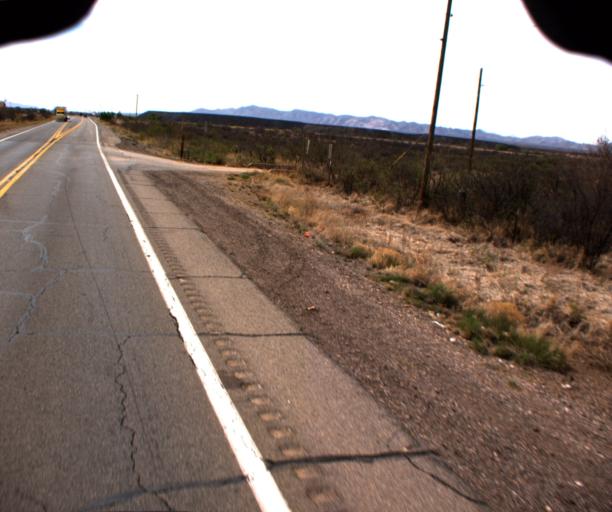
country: US
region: Arizona
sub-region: Cochise County
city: Pirtleville
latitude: 31.3580
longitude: -109.5795
